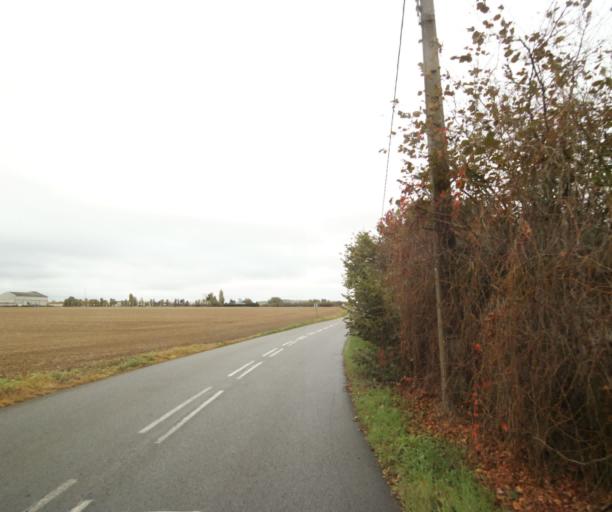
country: FR
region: Centre
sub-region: Departement d'Eure-et-Loir
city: Dreux
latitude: 48.7571
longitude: 1.3600
